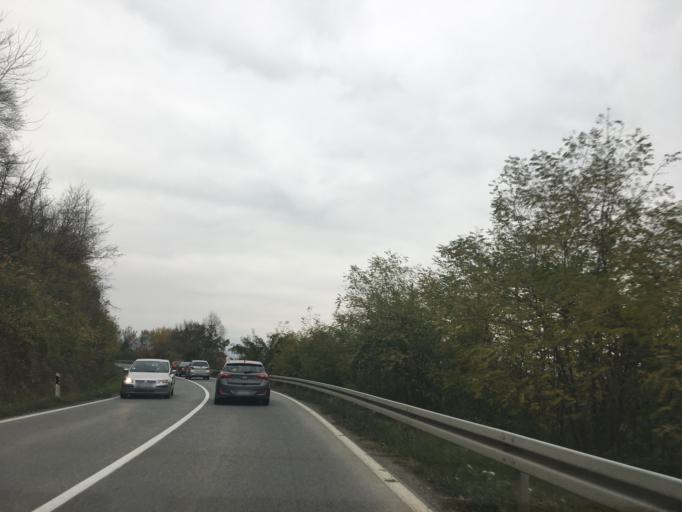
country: RS
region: Central Serbia
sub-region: Raski Okrug
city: Kraljevo
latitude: 43.7145
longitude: 20.7846
